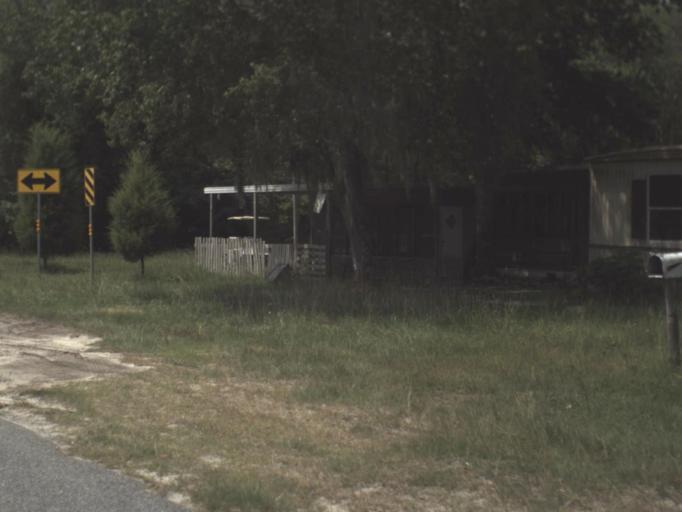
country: US
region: Georgia
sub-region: Echols County
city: Statenville
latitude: 30.6243
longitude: -83.1195
